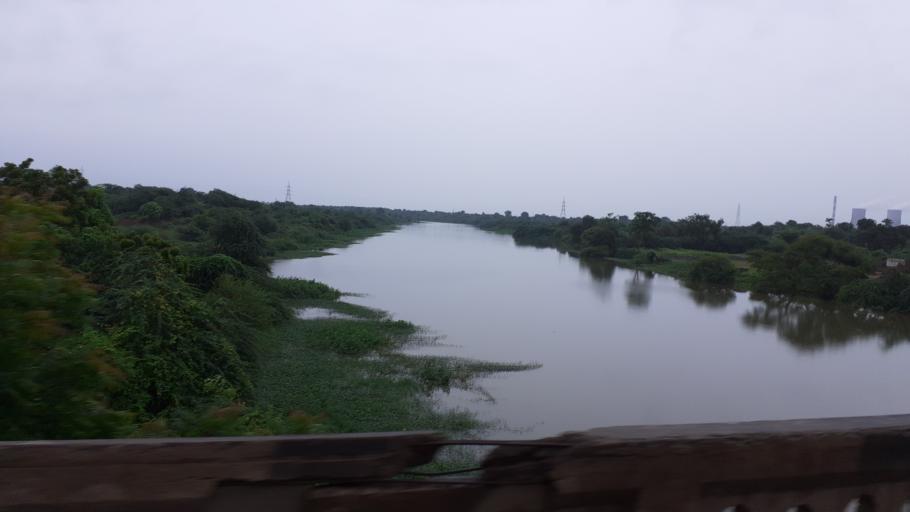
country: IN
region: Maharashtra
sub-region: Akola
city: Balapur
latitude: 20.6798
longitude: 76.7689
